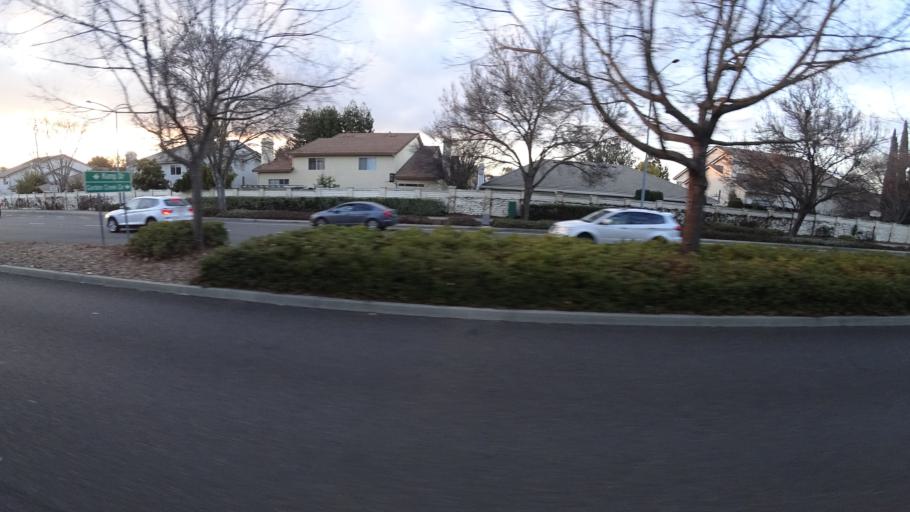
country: US
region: California
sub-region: Alameda County
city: Pleasanton
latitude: 37.6896
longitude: -121.8694
